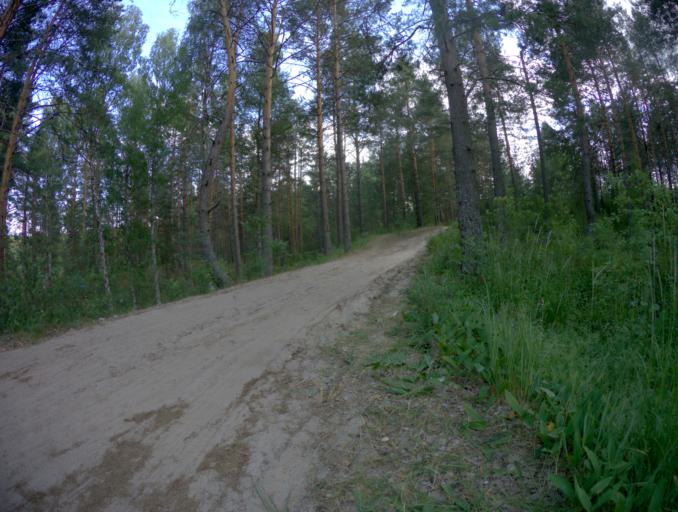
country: RU
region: Nizjnij Novgorod
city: Frolishchi
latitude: 56.3506
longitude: 42.7403
